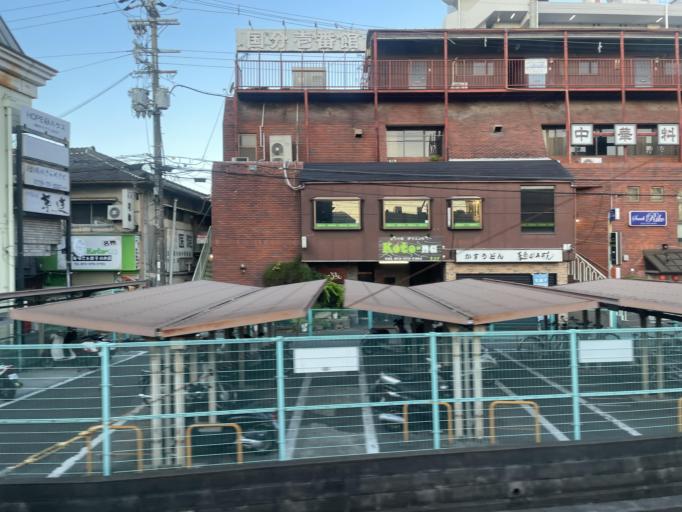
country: JP
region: Osaka
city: Kashihara
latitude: 34.5659
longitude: 135.6359
